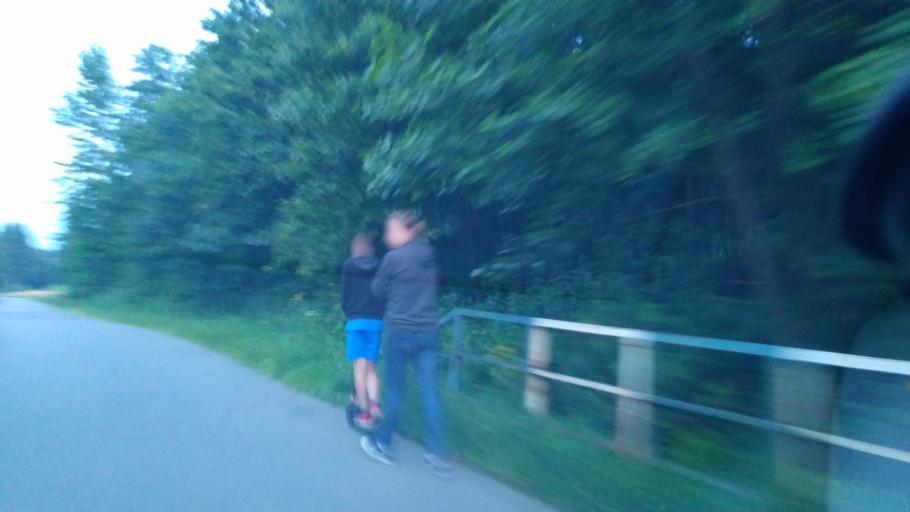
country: PL
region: Subcarpathian Voivodeship
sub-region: Powiat ropczycko-sedziszowski
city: Iwierzyce
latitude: 49.9920
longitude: 21.7253
